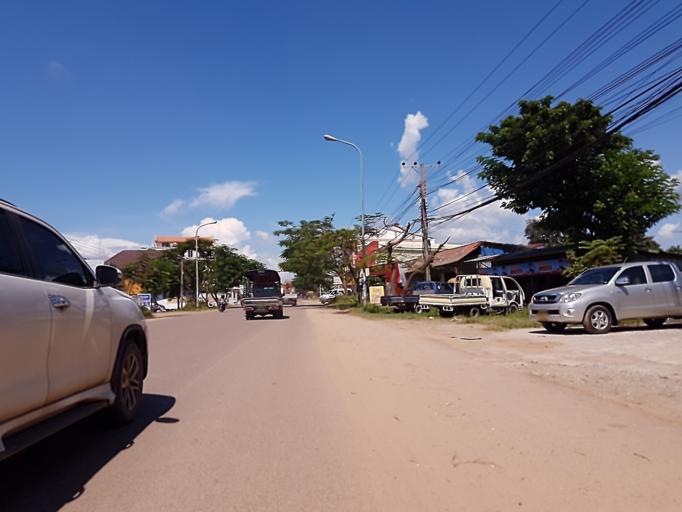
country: TH
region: Nong Khai
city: Tha Bo
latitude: 17.8968
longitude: 102.6463
